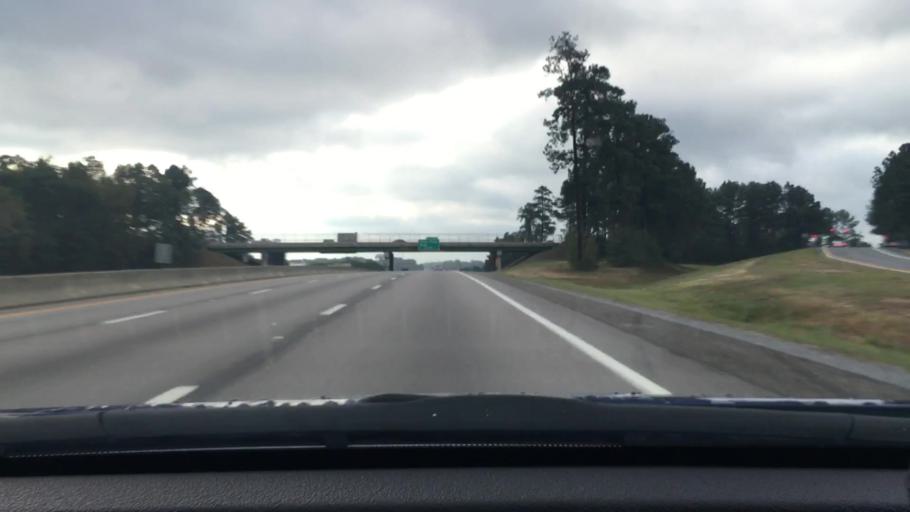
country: US
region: South Carolina
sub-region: Lexington County
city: Irmo
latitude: 34.0793
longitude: -81.1542
